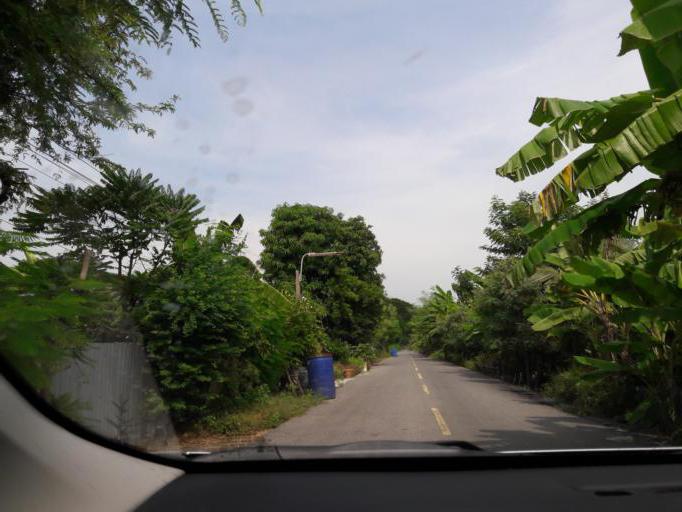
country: TH
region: Ang Thong
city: Ang Thong
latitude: 14.5780
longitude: 100.4544
